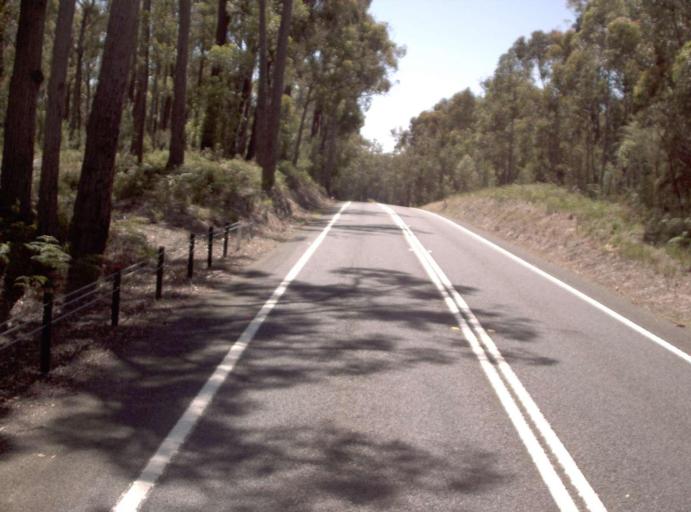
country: AU
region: Victoria
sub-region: East Gippsland
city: Lakes Entrance
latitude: -37.8157
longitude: 148.0288
